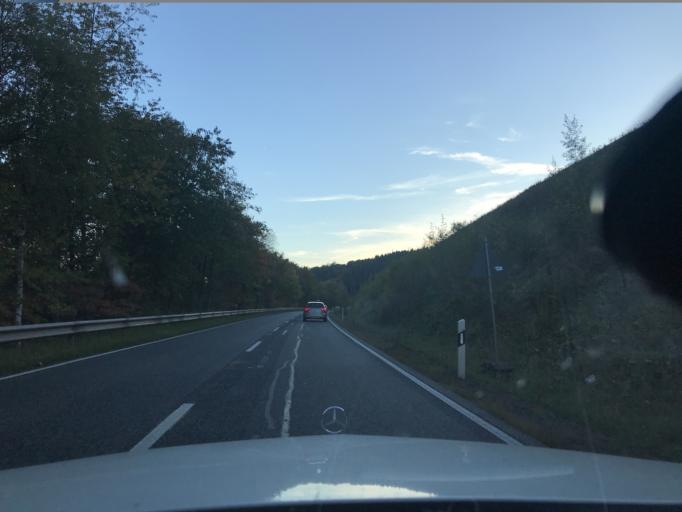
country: DE
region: Hesse
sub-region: Regierungsbezirk Kassel
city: Helsa
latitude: 51.2406
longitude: 9.6787
